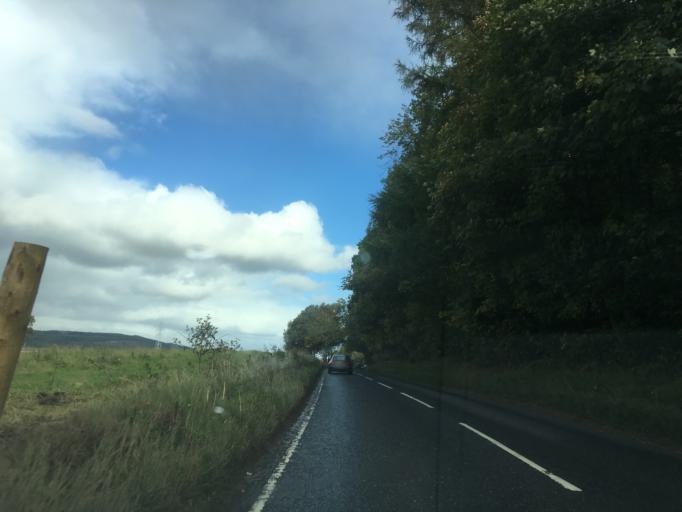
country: GB
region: Scotland
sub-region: Highland
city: Beauly
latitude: 57.4731
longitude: -4.3797
